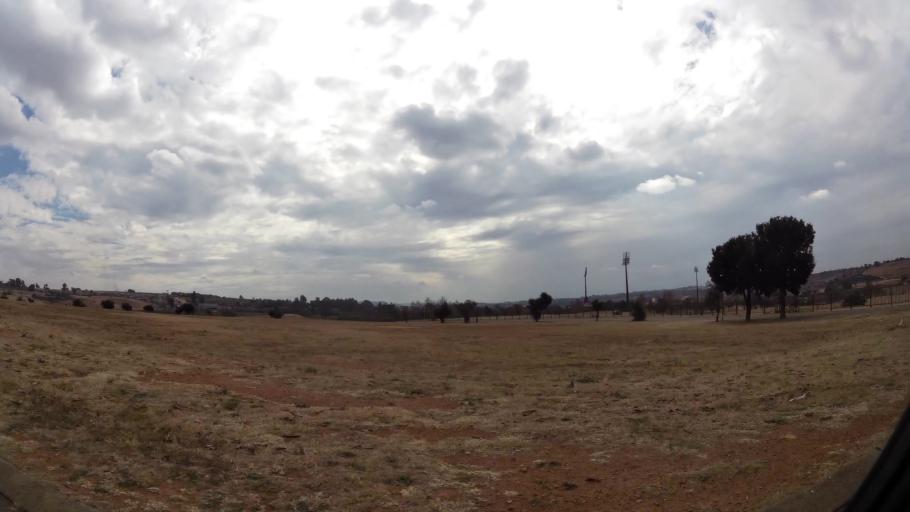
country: ZA
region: Gauteng
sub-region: West Rand District Municipality
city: Muldersdriseloop
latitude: -26.0753
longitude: 27.8653
